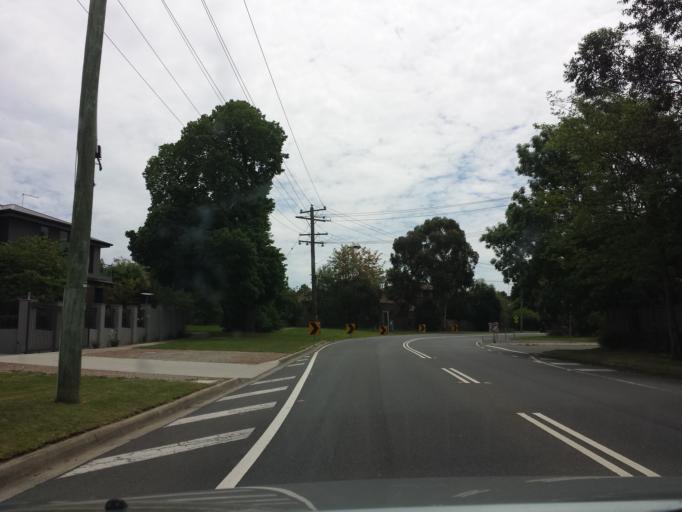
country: AU
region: Victoria
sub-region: Casey
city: Berwick
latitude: -38.0239
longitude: 145.3458
